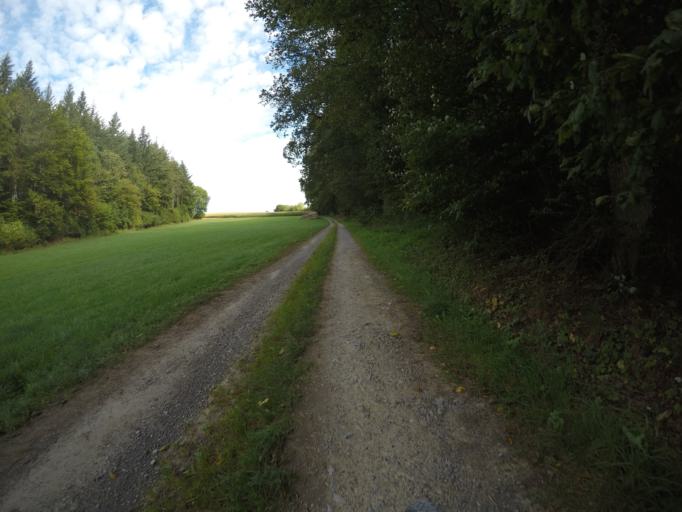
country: DE
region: Baden-Wuerttemberg
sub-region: Regierungsbezirk Stuttgart
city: Eberdingen
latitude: 48.8439
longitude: 8.9687
